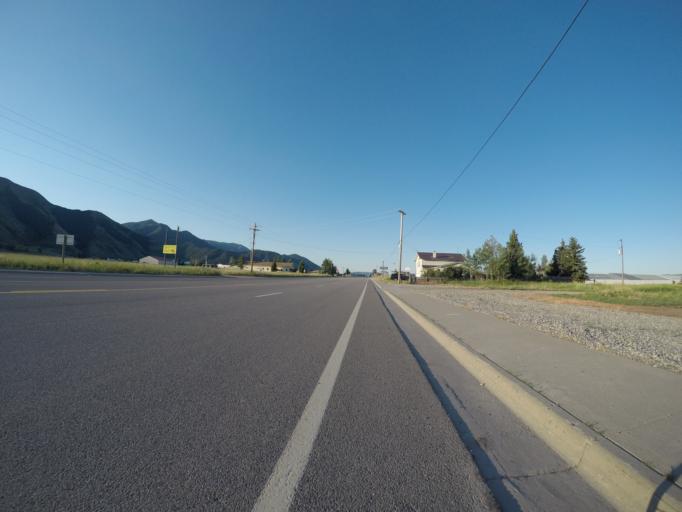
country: US
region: Wyoming
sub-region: Lincoln County
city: Afton
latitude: 42.7489
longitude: -110.9335
